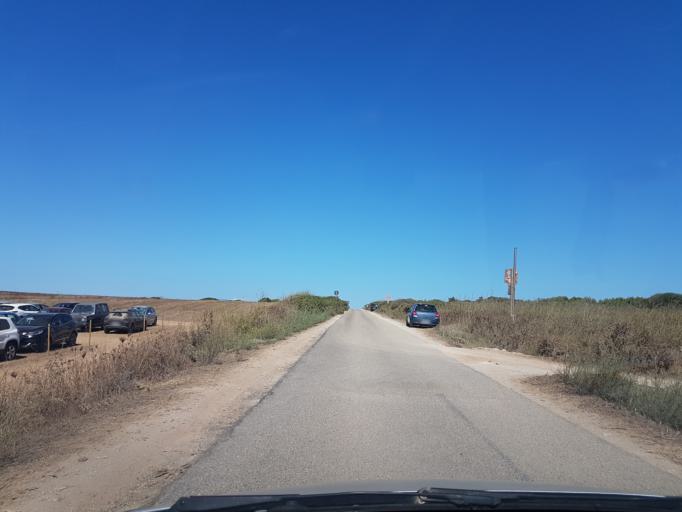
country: IT
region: Sardinia
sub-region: Provincia di Oristano
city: Cabras
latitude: 39.9693
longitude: 8.4015
